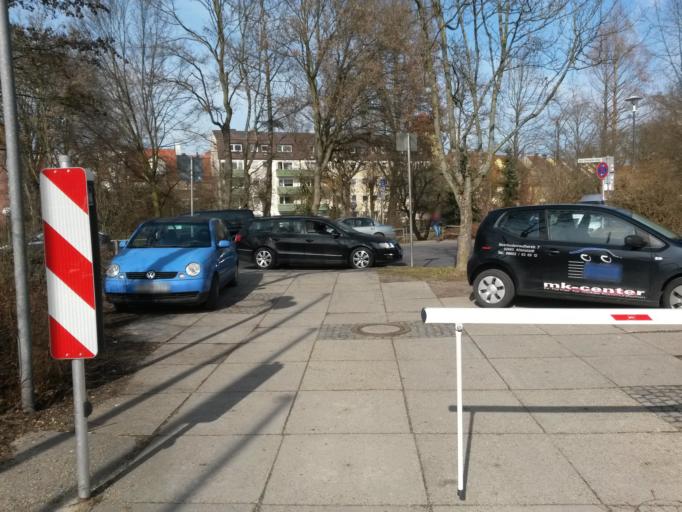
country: DE
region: Bavaria
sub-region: Upper Palatinate
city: Weiden
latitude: 49.6737
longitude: 12.1644
